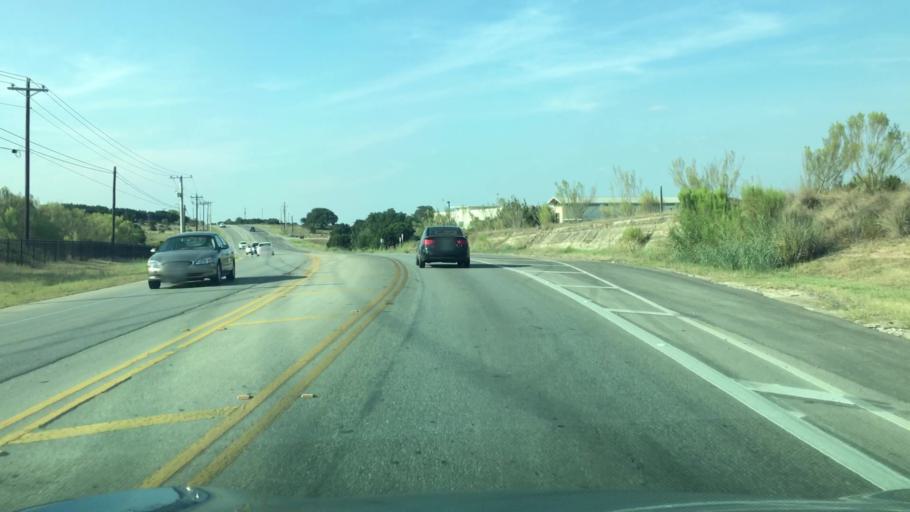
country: US
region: Texas
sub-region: Hays County
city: Dripping Springs
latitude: 30.1763
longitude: -98.0031
